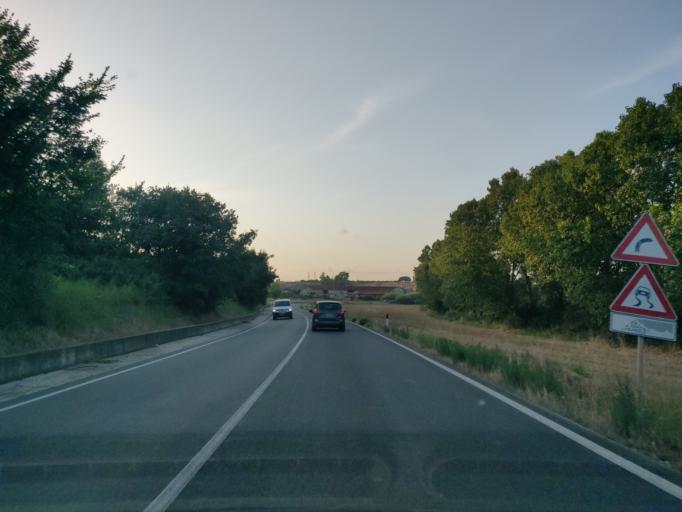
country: IT
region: Latium
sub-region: Citta metropolitana di Roma Capitale
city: Aurelia
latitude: 42.1477
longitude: 11.7887
